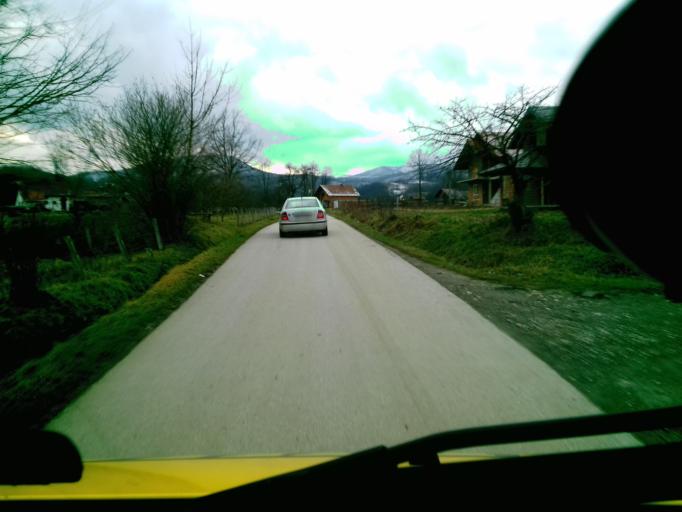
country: BA
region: Federation of Bosnia and Herzegovina
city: Lijesnica
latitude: 44.4762
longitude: 18.0495
